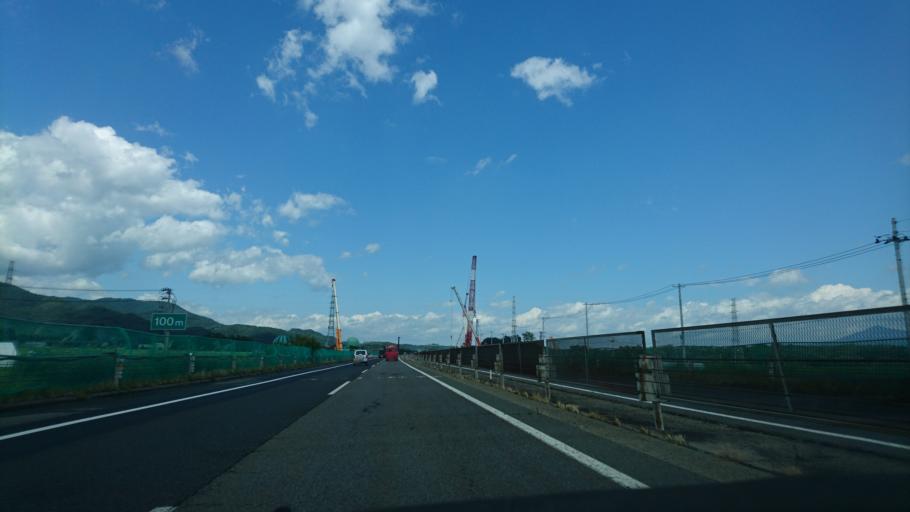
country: JP
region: Iwate
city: Morioka-shi
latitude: 39.7426
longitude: 141.0935
